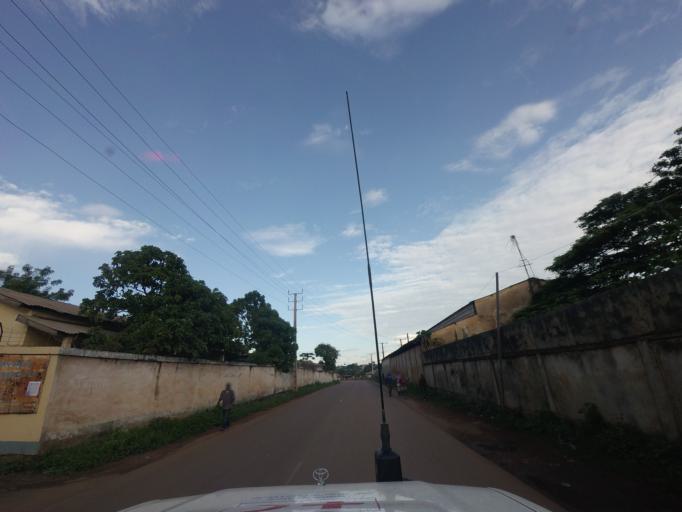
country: GN
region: Nzerekore
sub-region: Nzerekore Prefecture
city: Nzerekore
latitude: 7.7389
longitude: -8.8259
